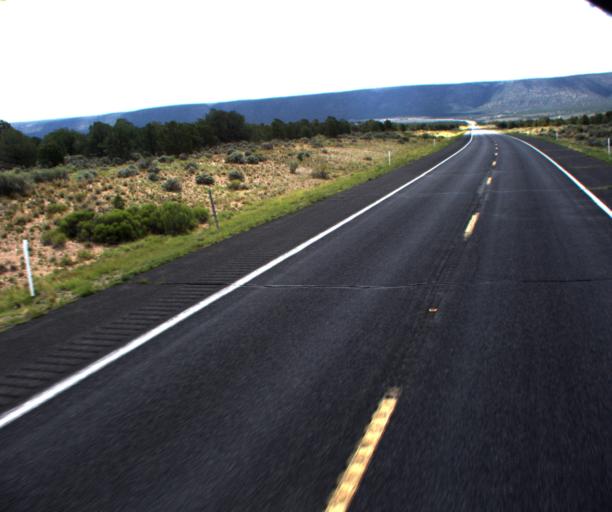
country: US
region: Arizona
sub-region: Coconino County
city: Grand Canyon
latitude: 35.9475
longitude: -111.7794
